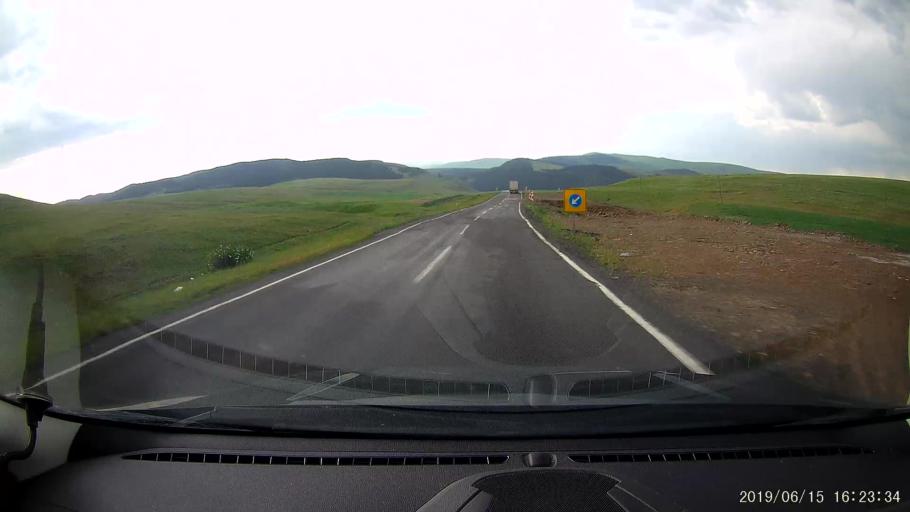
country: TR
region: Ardahan
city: Hanak
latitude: 41.1764
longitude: 42.8636
